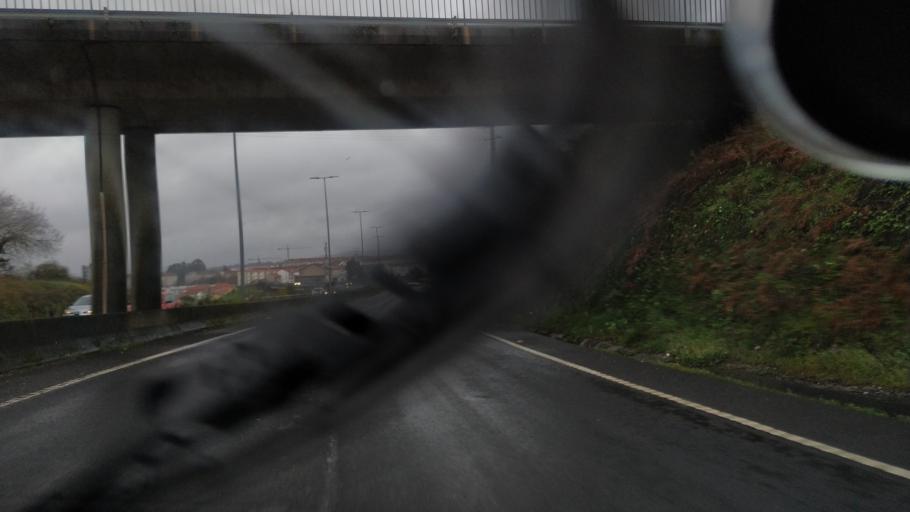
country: ES
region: Galicia
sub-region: Provincia da Coruna
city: Santiago de Compostela
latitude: 42.8603
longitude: -8.5466
